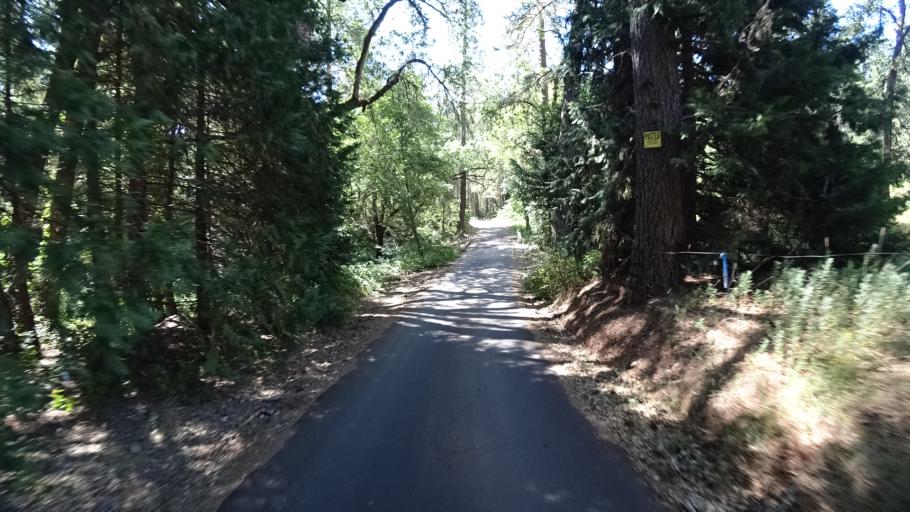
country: US
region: California
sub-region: Amador County
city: Pioneer
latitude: 38.3881
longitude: -120.5006
